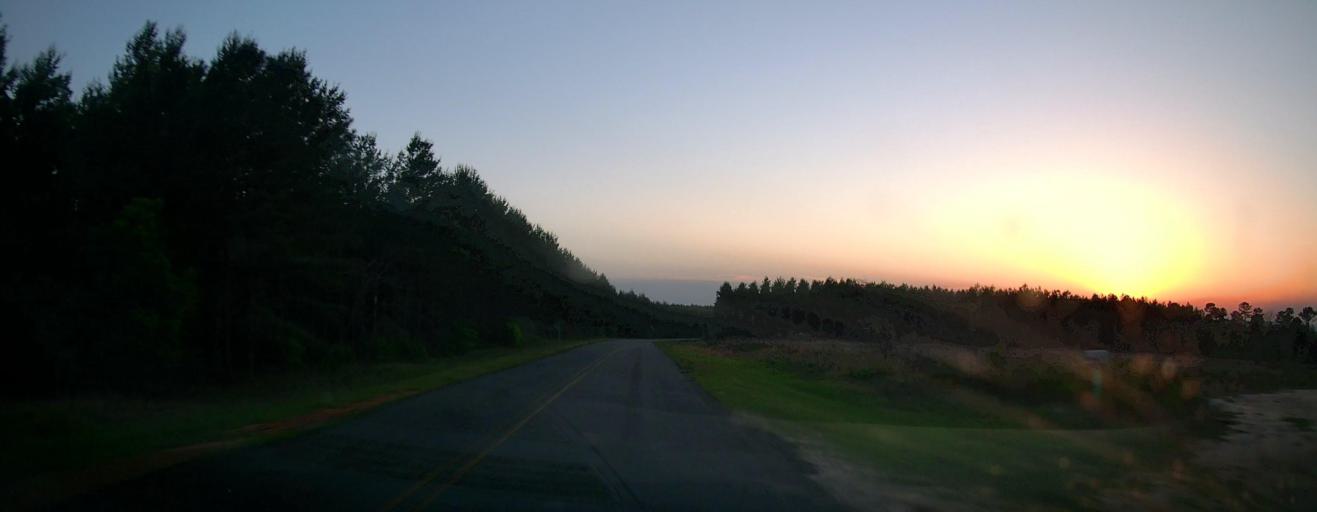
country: US
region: Georgia
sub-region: Marion County
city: Buena Vista
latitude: 32.2604
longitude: -84.5629
